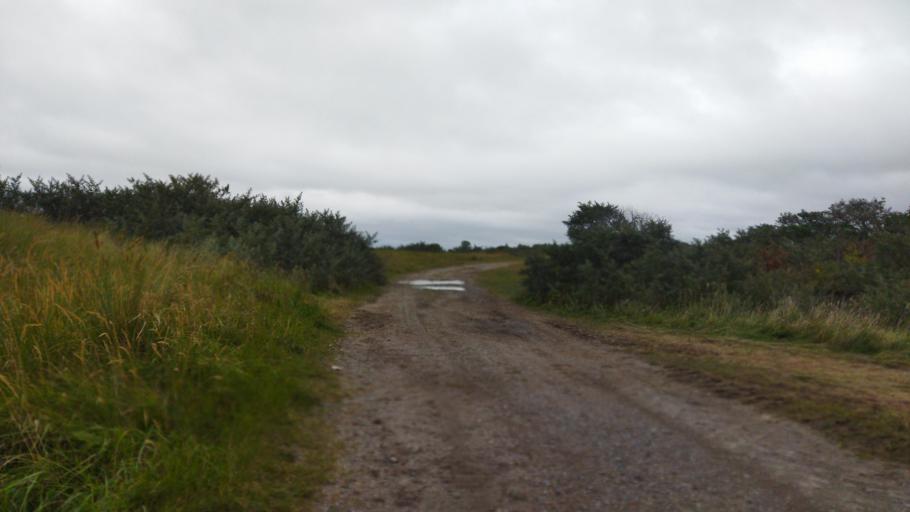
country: NL
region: Groningen
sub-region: Gemeente Delfzijl
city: Delfzijl
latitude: 53.3603
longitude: 7.0010
